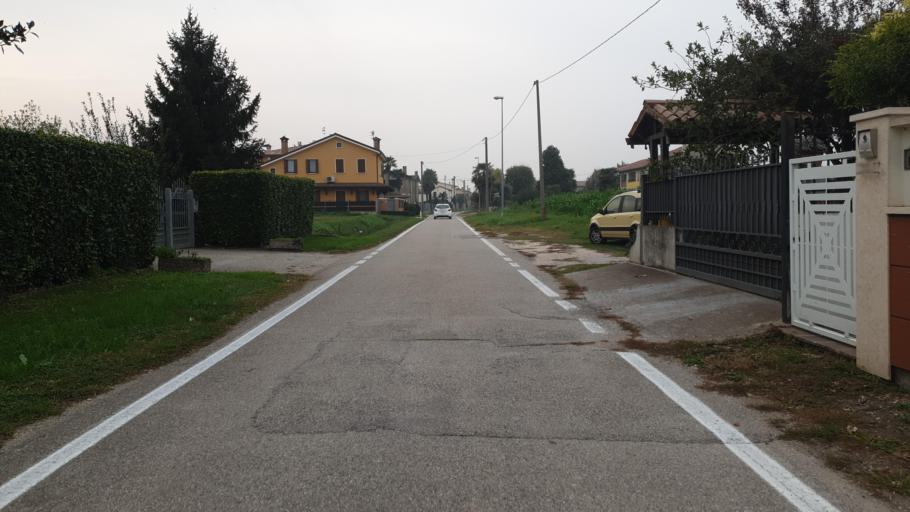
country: IT
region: Veneto
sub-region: Provincia di Padova
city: Bertipaglia
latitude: 45.3200
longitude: 11.8920
